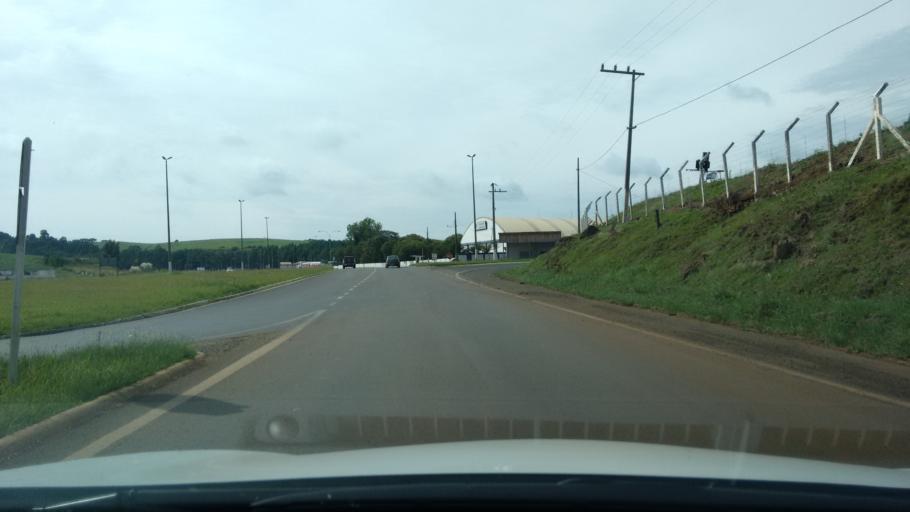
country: BR
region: Santa Catarina
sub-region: Curitibanos
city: Curitibanos
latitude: -27.3128
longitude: -50.5779
